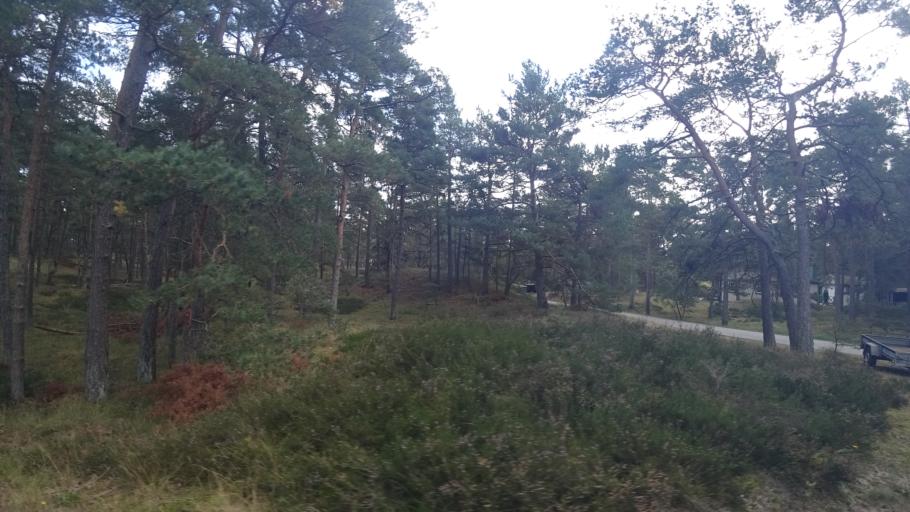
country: SE
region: Skane
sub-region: Kristianstads Kommun
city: Ahus
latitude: 55.9134
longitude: 14.2899
